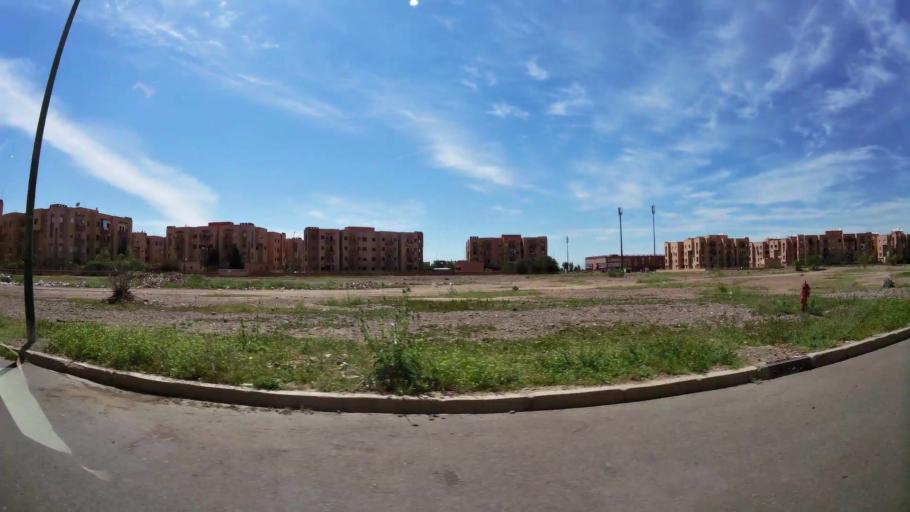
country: MA
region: Marrakech-Tensift-Al Haouz
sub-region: Marrakech
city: Marrakesh
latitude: 31.6432
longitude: -8.0789
